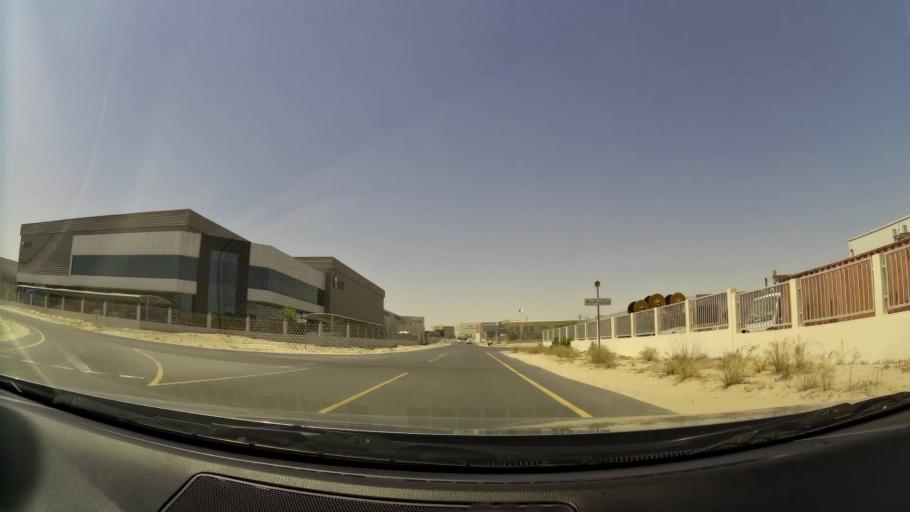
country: AE
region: Dubai
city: Dubai
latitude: 24.9780
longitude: 55.1902
